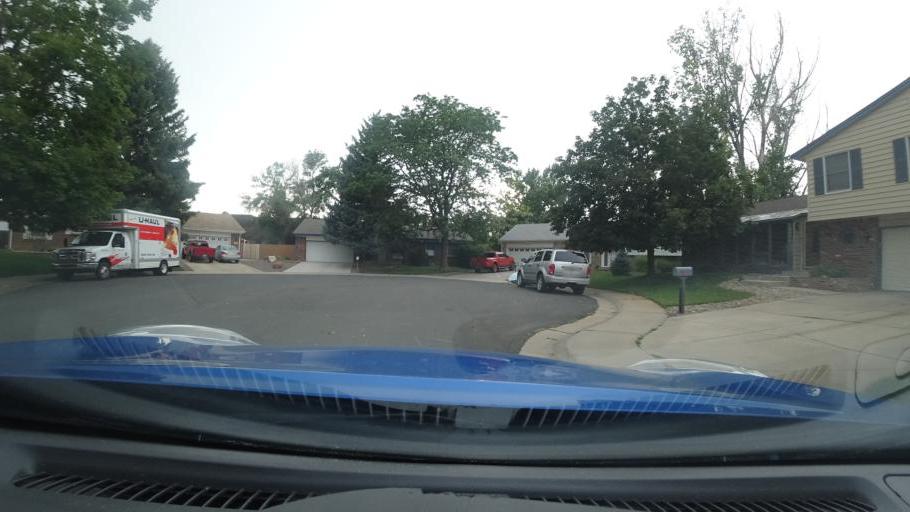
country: US
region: Colorado
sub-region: Adams County
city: Aurora
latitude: 39.6937
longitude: -104.8253
